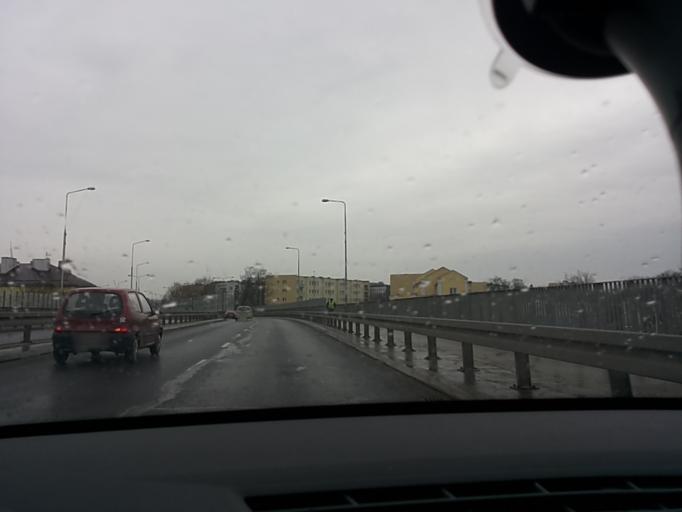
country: PL
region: Lodz Voivodeship
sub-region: Skierniewice
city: Skierniewice
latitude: 51.9671
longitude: 20.1511
